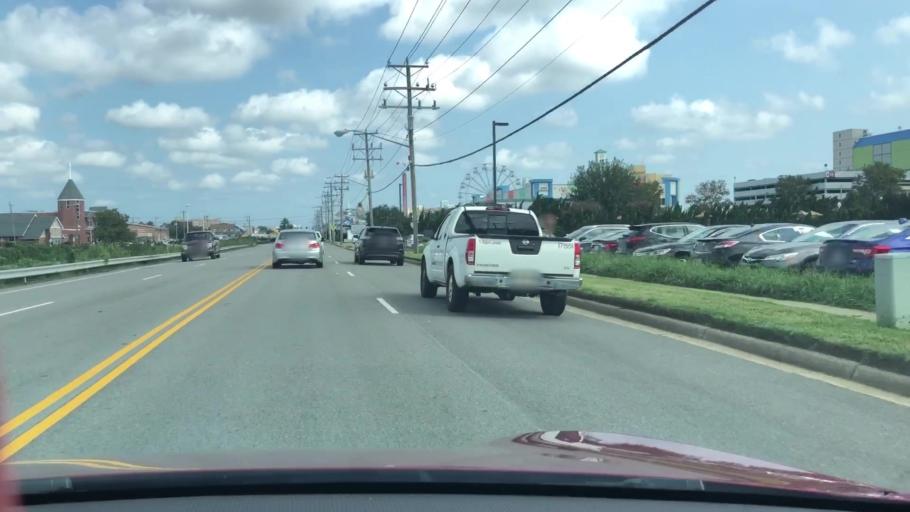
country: US
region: Virginia
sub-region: City of Virginia Beach
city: Virginia Beach
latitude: 36.8405
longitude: -75.9743
